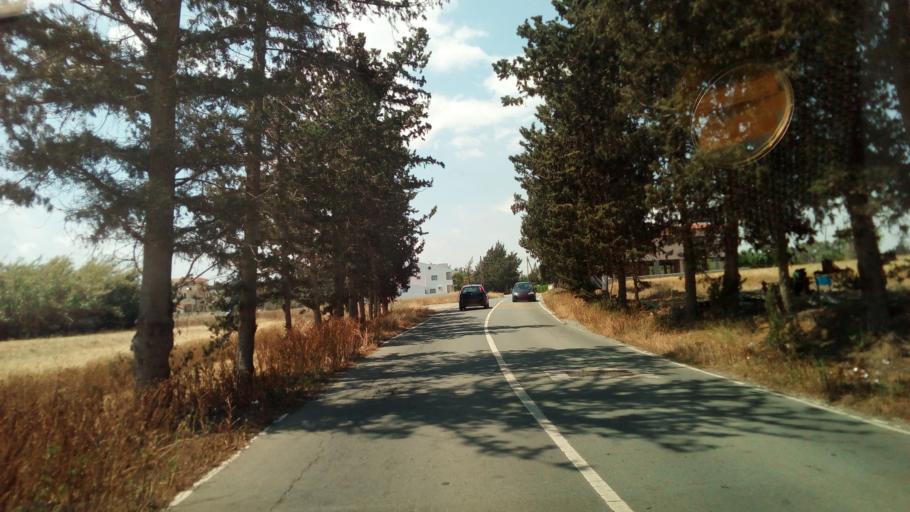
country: CY
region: Larnaka
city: Meneou
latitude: 34.8564
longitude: 33.6000
